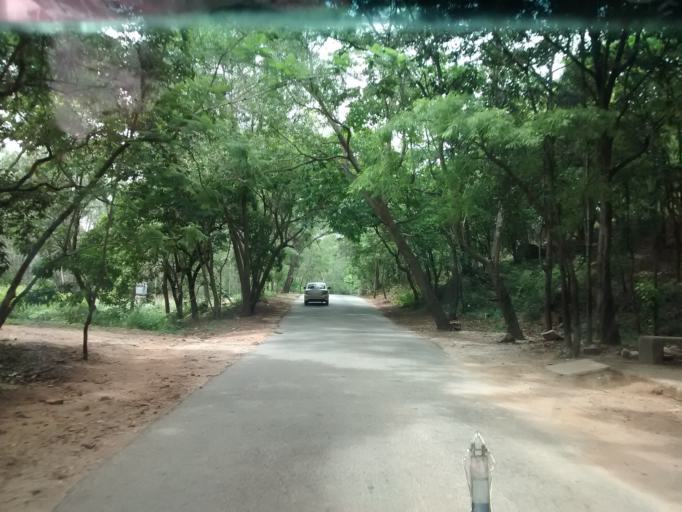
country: IN
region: Andhra Pradesh
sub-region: Chittoor
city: Tirumala
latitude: 13.7026
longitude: 79.3408
